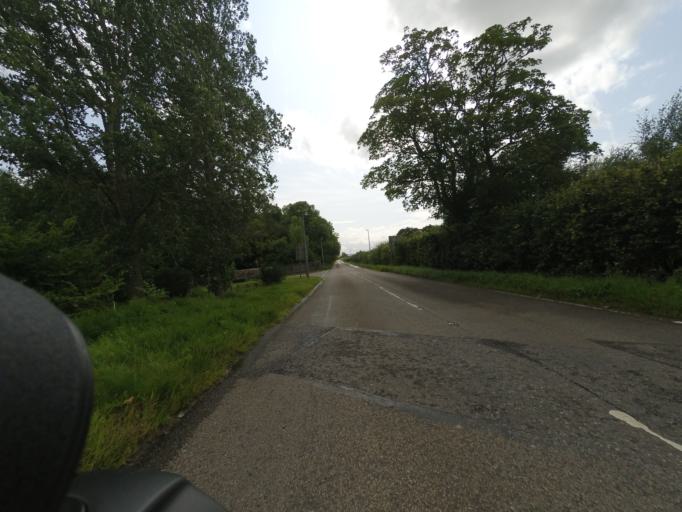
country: GB
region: Scotland
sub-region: Highland
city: Tain
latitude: 57.7402
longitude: -4.0795
